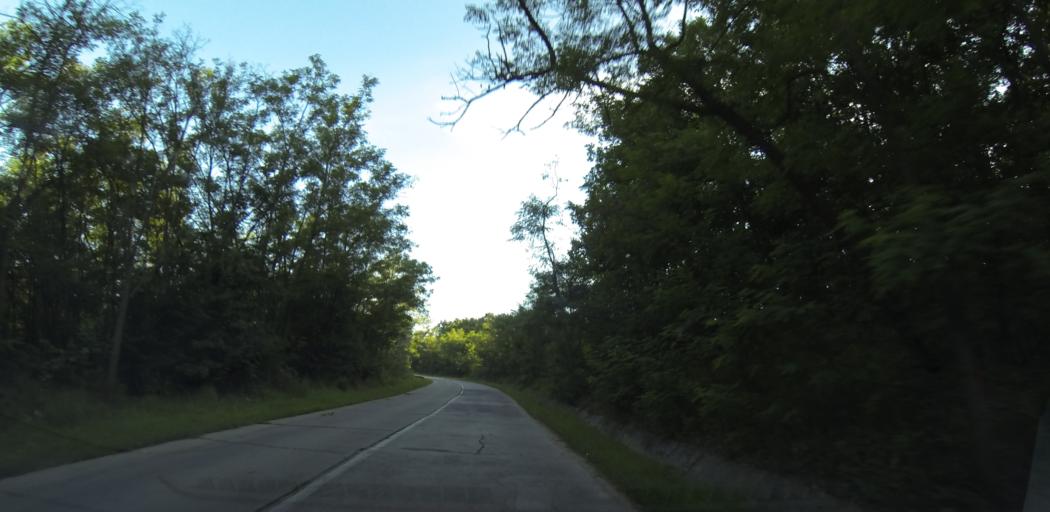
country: RO
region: Valcea
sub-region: Comuna Balcesti
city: Balcesti
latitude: 44.5900
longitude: 23.9221
